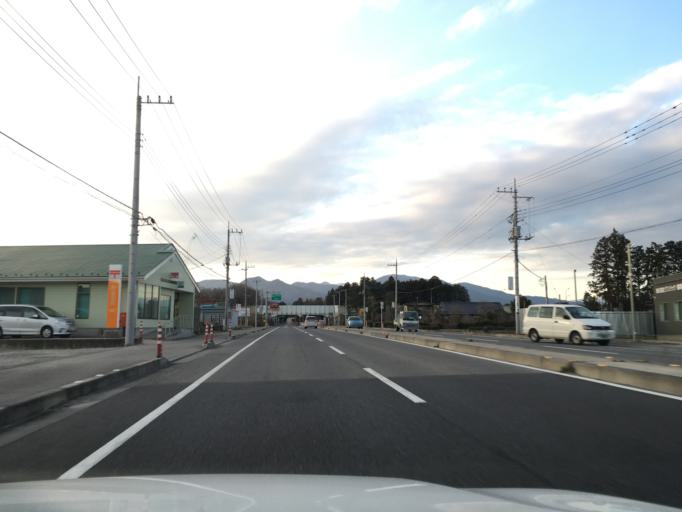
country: JP
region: Tochigi
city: Otawara
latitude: 36.9128
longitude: 139.9428
